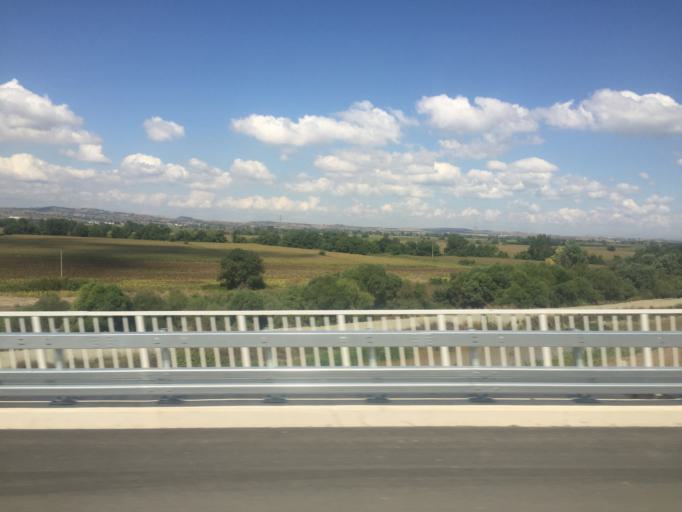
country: TR
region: Balikesir
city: Gobel
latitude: 40.0308
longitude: 28.2129
